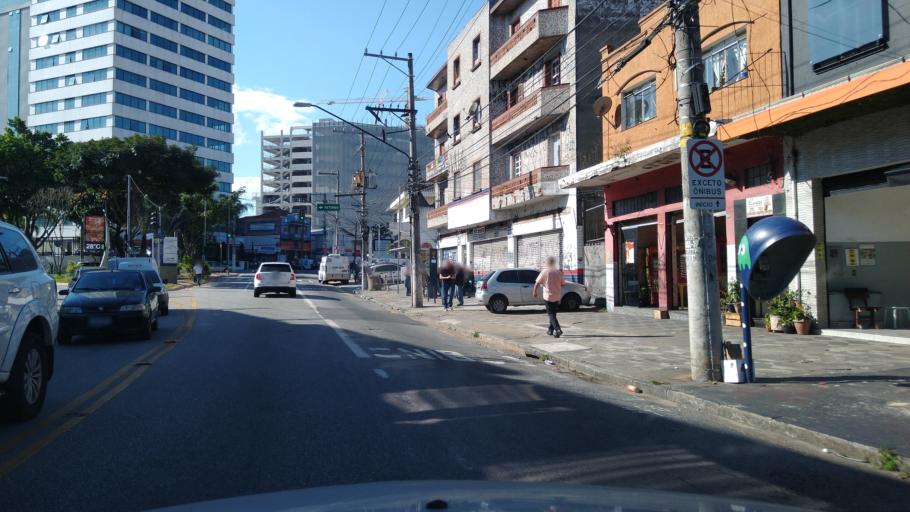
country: BR
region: Sao Paulo
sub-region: Sao Paulo
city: Sao Paulo
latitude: -23.4806
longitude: -46.6113
